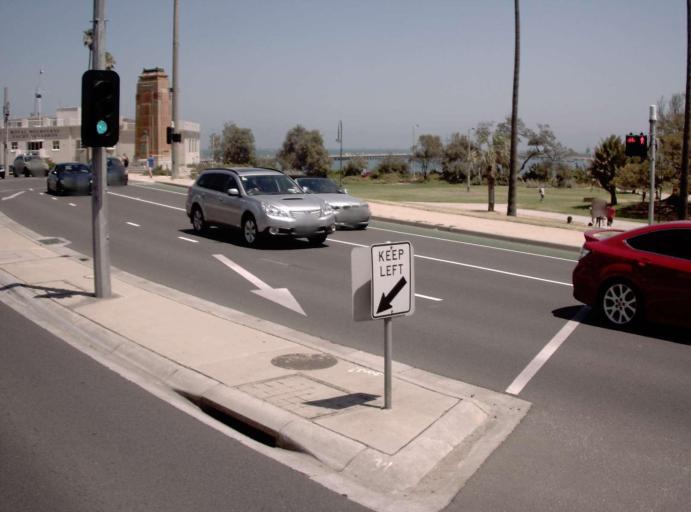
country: AU
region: Victoria
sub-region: Port Phillip
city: St Kilda West
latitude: -37.8623
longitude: 144.9728
